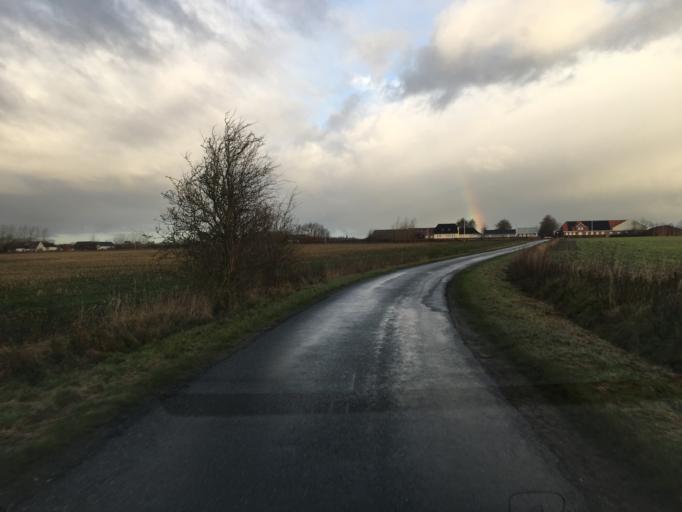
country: DK
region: South Denmark
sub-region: Tonder Kommune
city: Sherrebek
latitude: 55.1531
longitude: 8.8260
